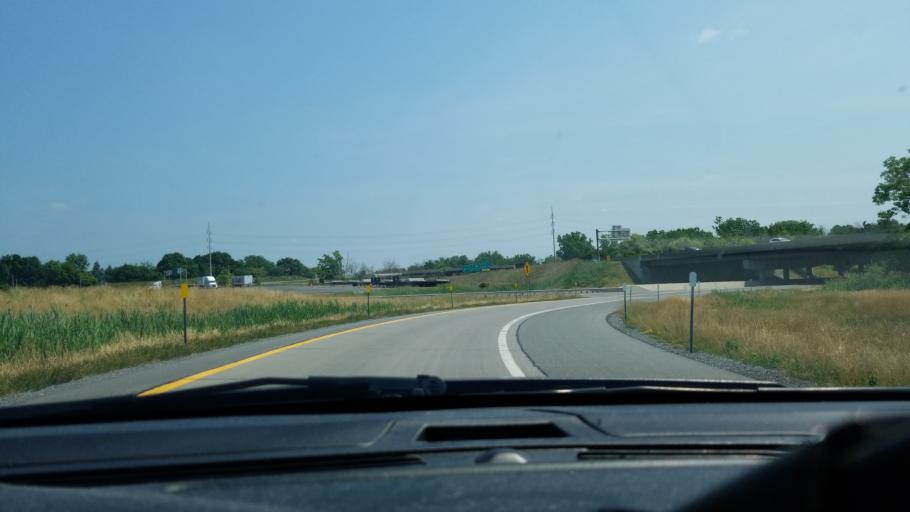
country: US
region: New York
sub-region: Onondaga County
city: Galeville
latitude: 43.0928
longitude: -76.1656
